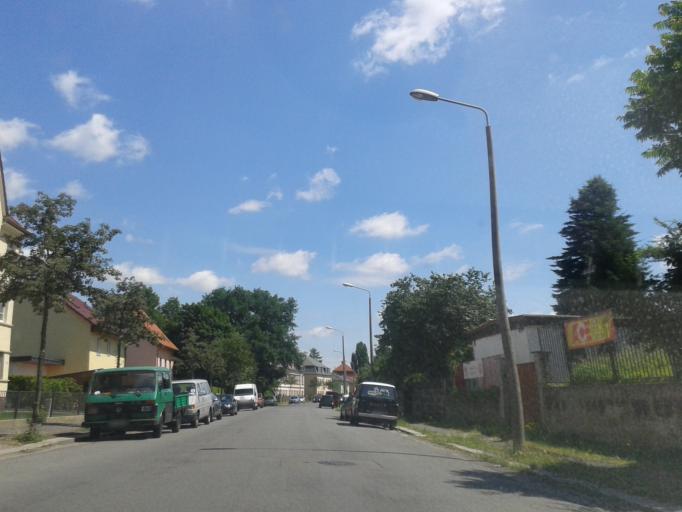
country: DE
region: Saxony
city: Radebeul
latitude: 51.0740
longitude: 13.6937
